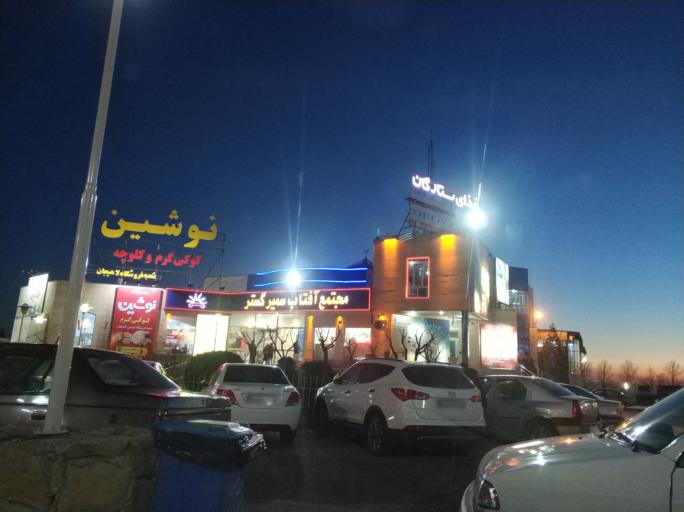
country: IR
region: Qazvin
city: Alvand
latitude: 36.2346
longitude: 50.1738
